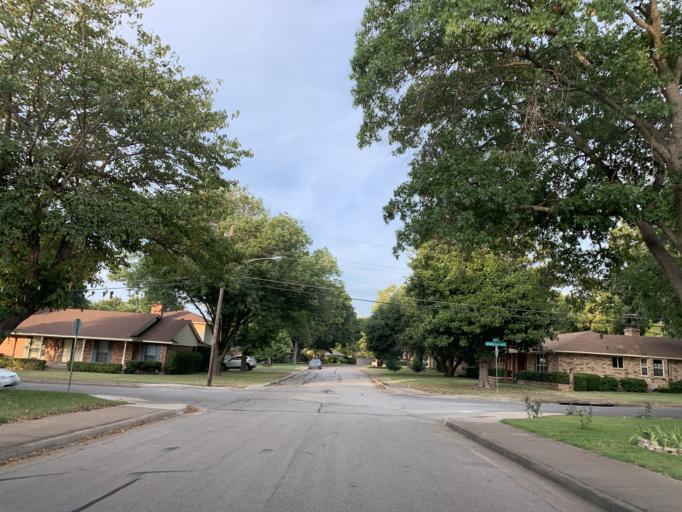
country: US
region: Texas
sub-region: Dallas County
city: Cockrell Hill
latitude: 32.6962
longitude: -96.8858
